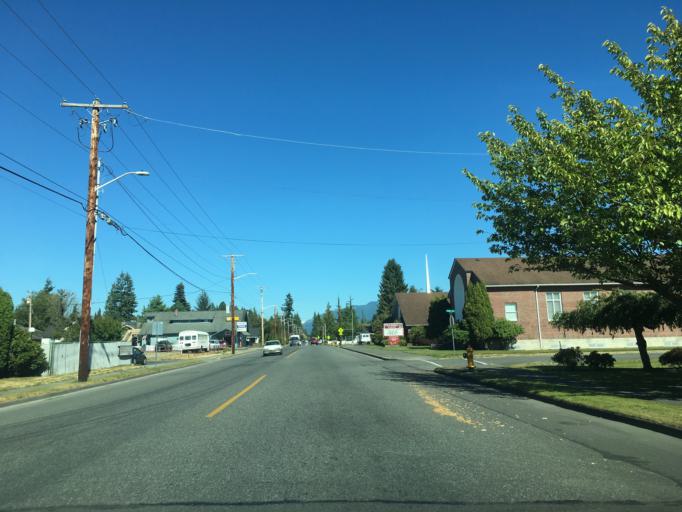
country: US
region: Washington
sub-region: Skagit County
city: Sedro-Woolley
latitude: 48.5033
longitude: -122.2341
